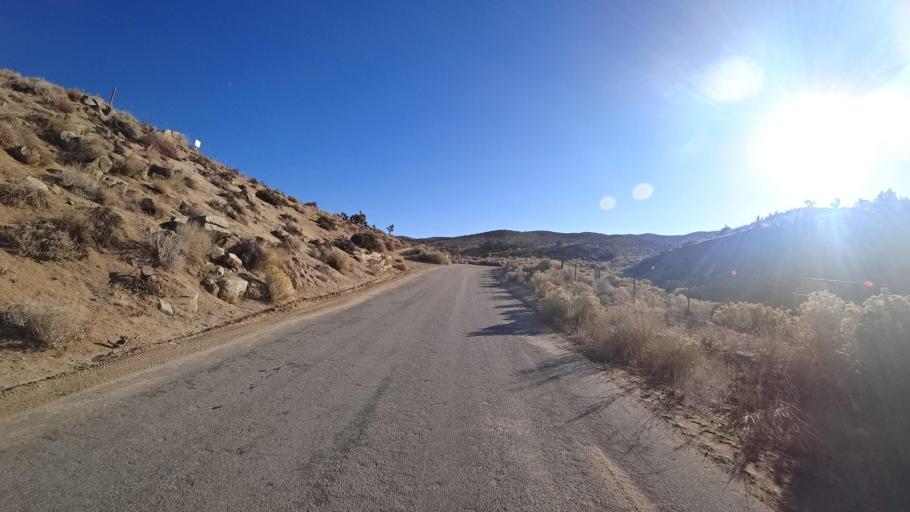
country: US
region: California
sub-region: Kern County
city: Weldon
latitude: 35.4620
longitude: -118.2115
